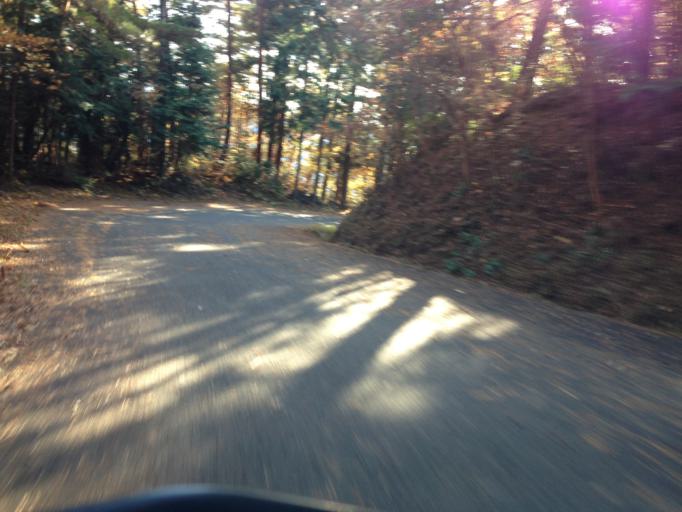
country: JP
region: Gifu
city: Mitake
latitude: 35.6133
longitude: 137.2156
